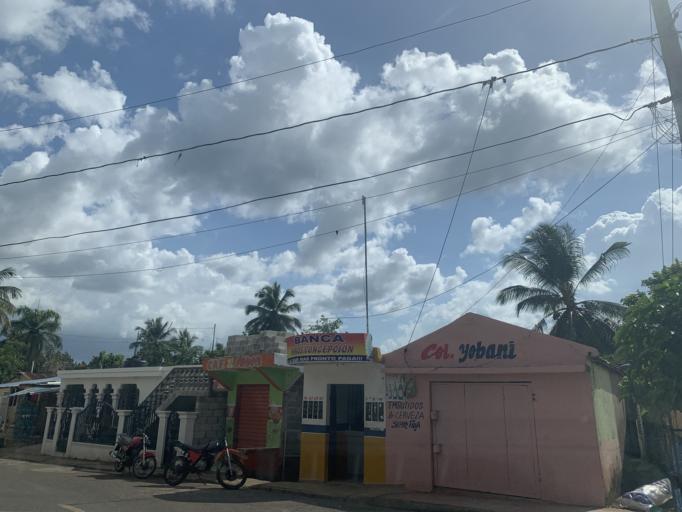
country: DO
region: Monte Plata
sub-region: Yamasa
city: Yamasa
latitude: 18.7754
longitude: -70.0285
